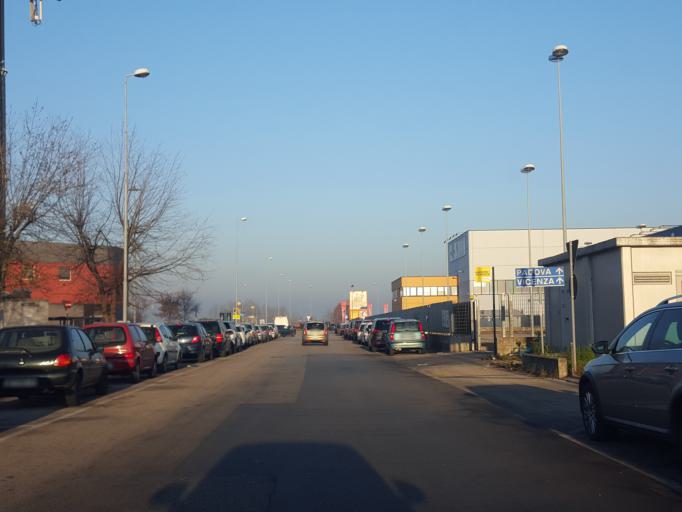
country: IT
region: Veneto
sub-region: Provincia di Vicenza
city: Torri di Quartesolo
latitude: 45.5083
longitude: 11.6262
